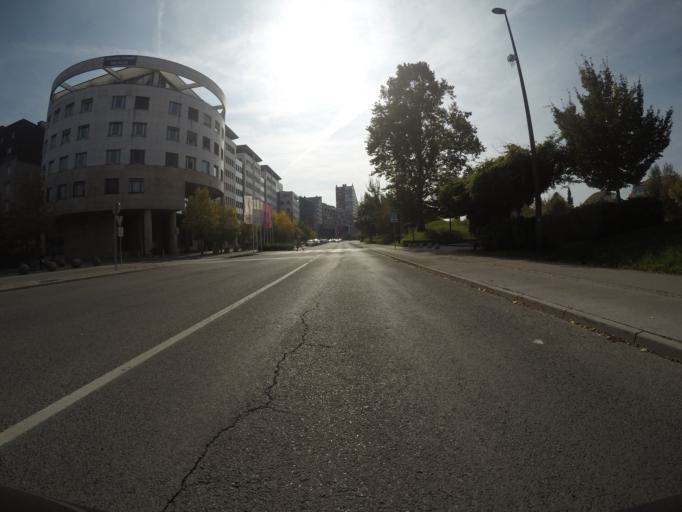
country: SI
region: Ljubljana
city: Ljubljana
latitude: 46.0634
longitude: 14.5130
